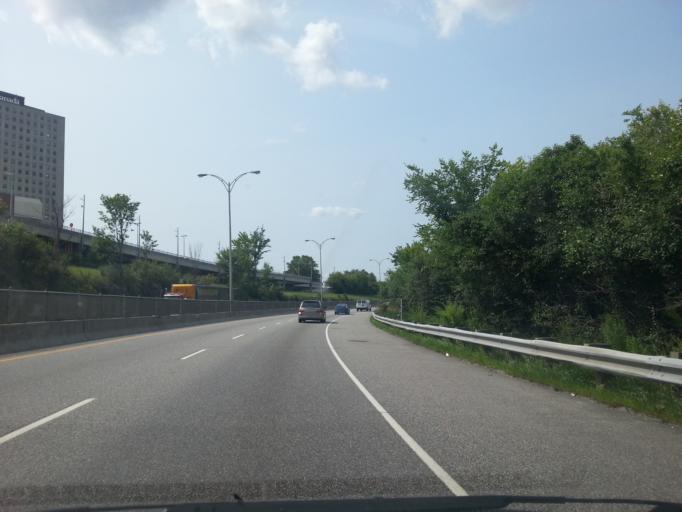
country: CA
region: Ontario
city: Ottawa
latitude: 45.4419
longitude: -75.7302
